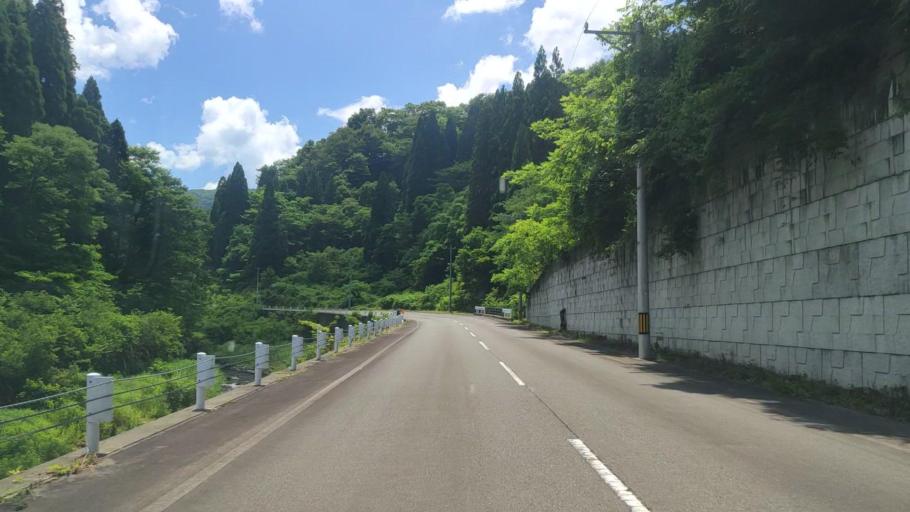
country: JP
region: Fukui
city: Ono
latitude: 35.8365
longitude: 136.4446
